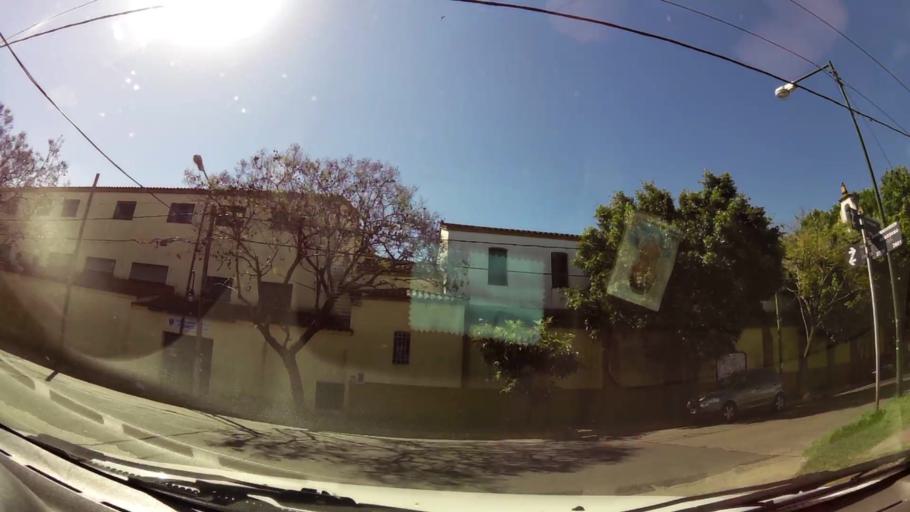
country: AR
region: Buenos Aires
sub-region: Partido de San Isidro
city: San Isidro
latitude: -34.4527
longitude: -58.5282
